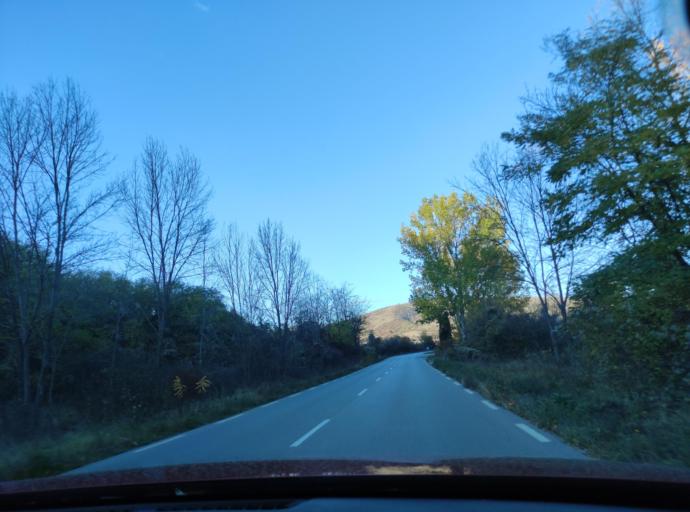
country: BG
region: Montana
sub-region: Obshtina Montana
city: Montana
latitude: 43.3986
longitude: 23.1293
